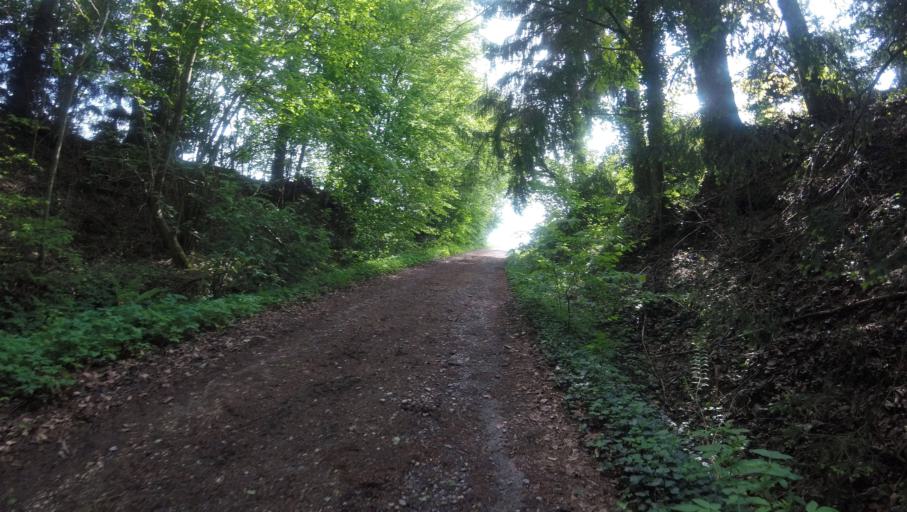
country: DE
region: Baden-Wuerttemberg
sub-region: Regierungsbezirk Stuttgart
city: Kaisersbach
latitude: 48.9149
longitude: 9.6159
